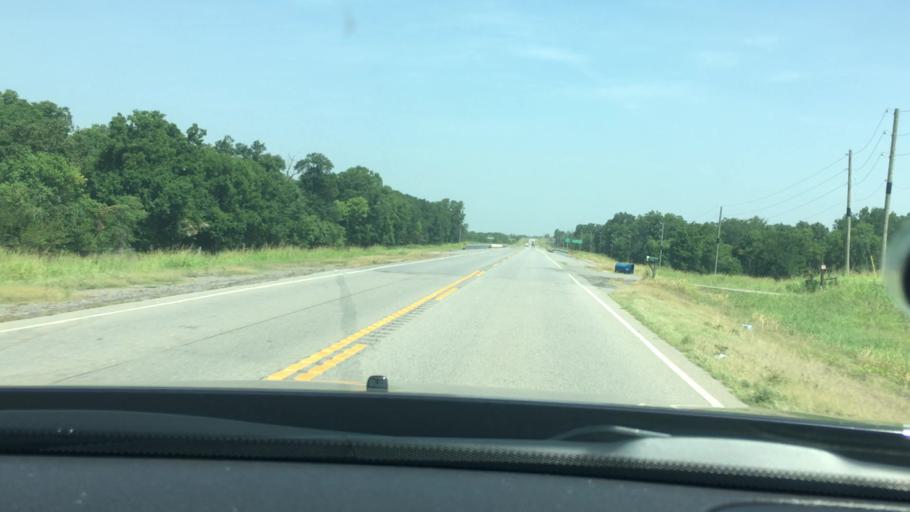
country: US
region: Oklahoma
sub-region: Coal County
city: Coalgate
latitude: 34.4437
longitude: -96.2056
